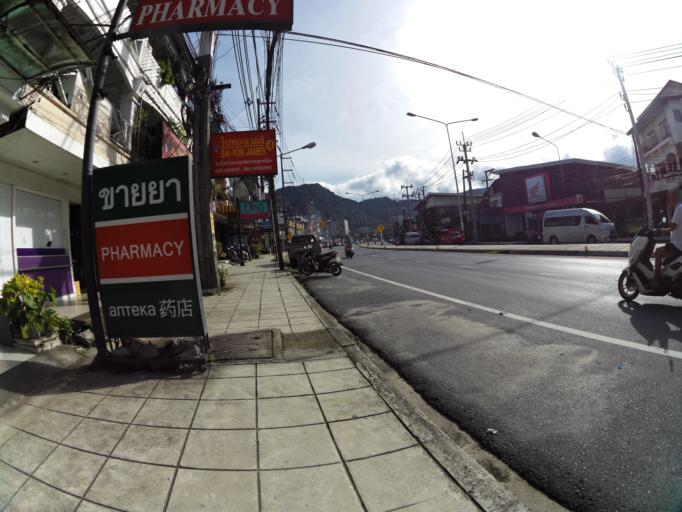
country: TH
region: Phuket
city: Patong
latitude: 7.9476
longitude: 98.2814
